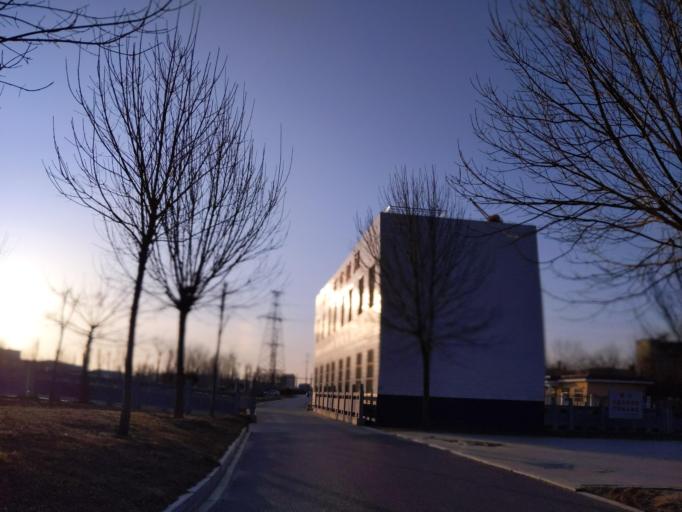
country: CN
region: Henan Sheng
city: Puyang
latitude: 35.7708
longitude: 114.9955
